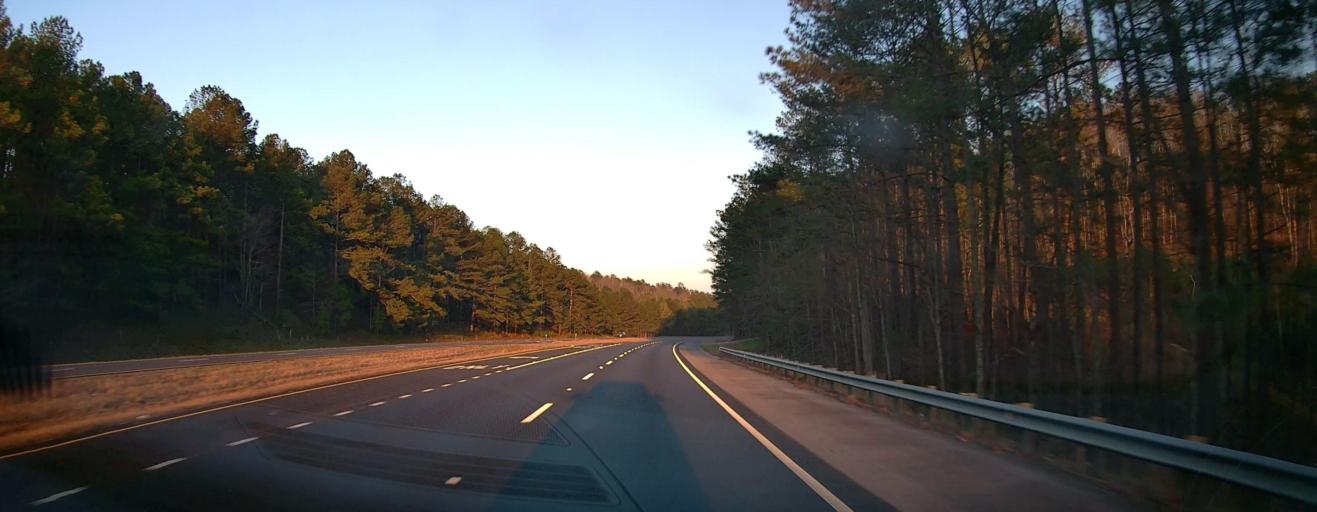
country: US
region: Alabama
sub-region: Coosa County
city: Stewartville
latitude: 33.0747
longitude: -86.1699
